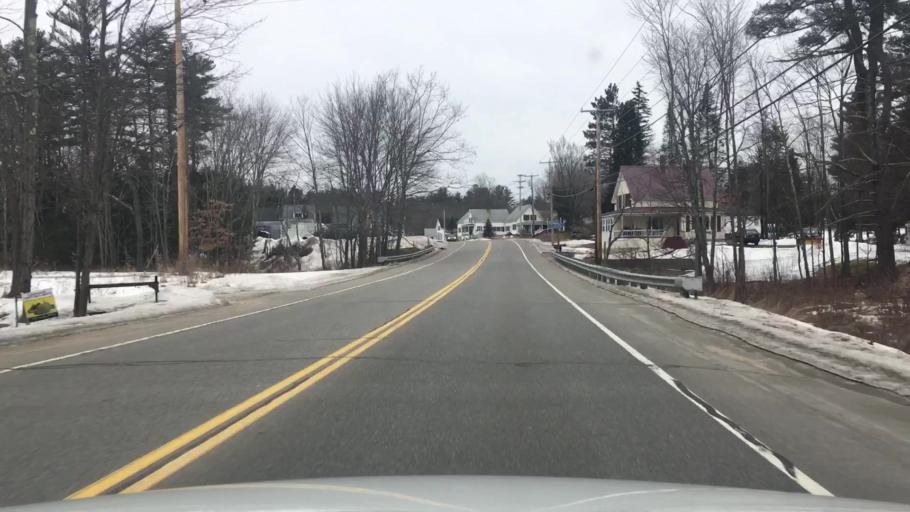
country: US
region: Maine
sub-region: York County
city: Springvale
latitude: 43.4745
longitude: -70.8108
